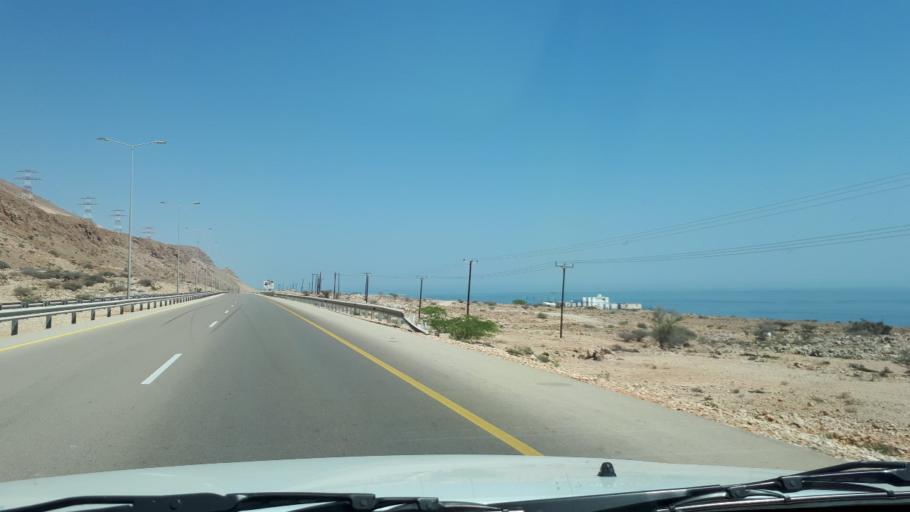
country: OM
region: Ash Sharqiyah
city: Sur
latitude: 22.7998
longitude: 59.2710
